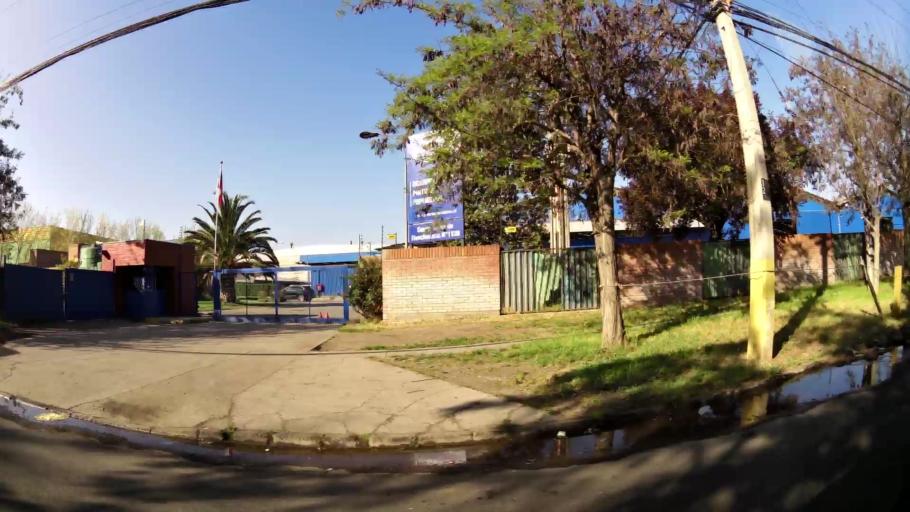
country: CL
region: Santiago Metropolitan
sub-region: Provincia de Chacabuco
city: Chicureo Abajo
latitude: -33.3693
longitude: -70.6619
